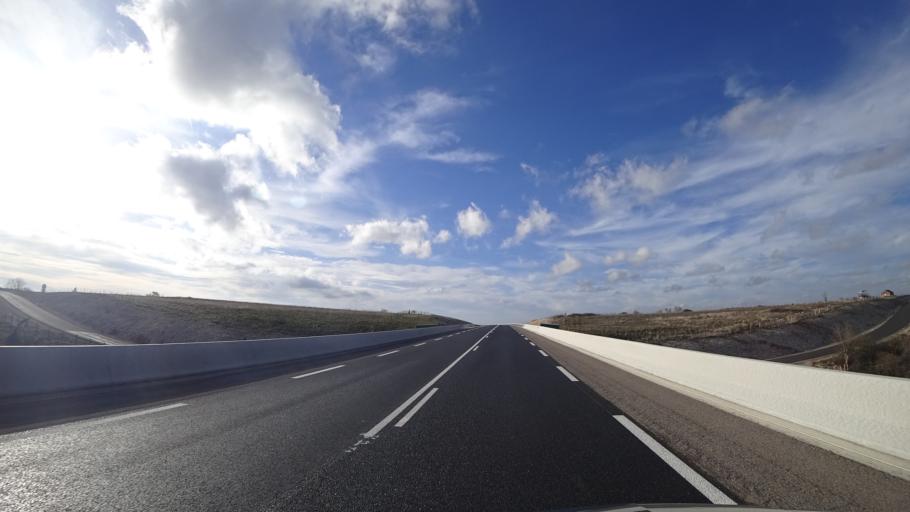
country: FR
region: Midi-Pyrenees
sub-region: Departement de l'Aveyron
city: Sebazac-Concoures
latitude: 44.4163
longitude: 2.6448
